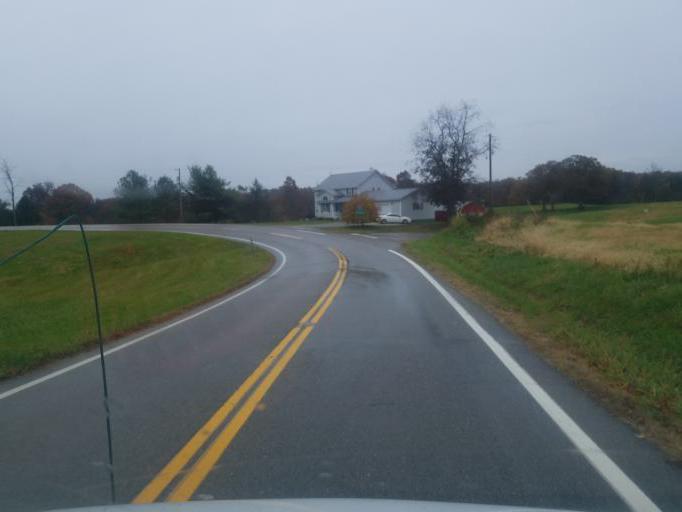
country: US
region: Ohio
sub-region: Washington County
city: Beverly
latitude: 39.4671
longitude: -81.6576
